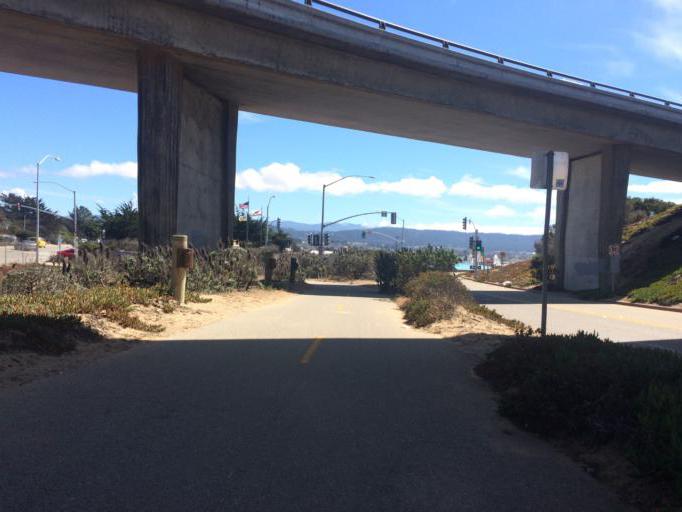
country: US
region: California
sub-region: Monterey County
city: Seaside
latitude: 36.6244
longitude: -121.8417
